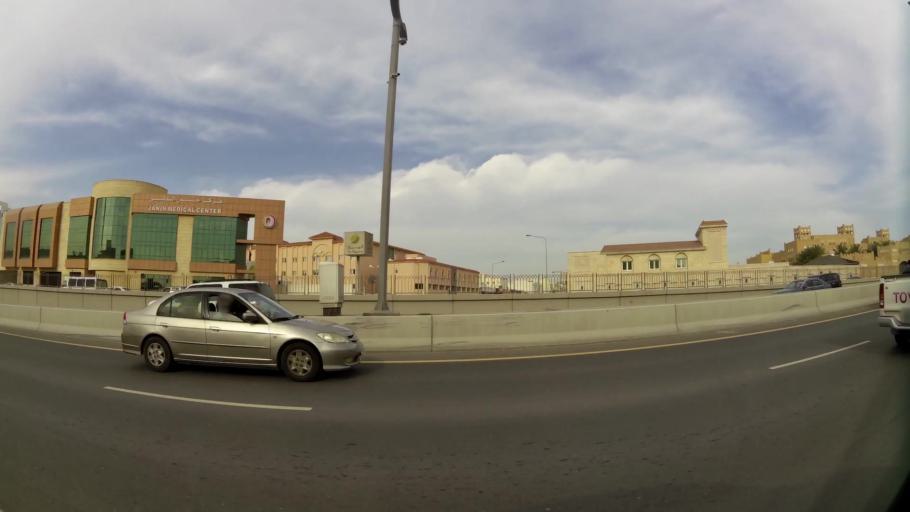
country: QA
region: Baladiyat ad Dawhah
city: Doha
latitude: 25.2725
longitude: 51.4910
